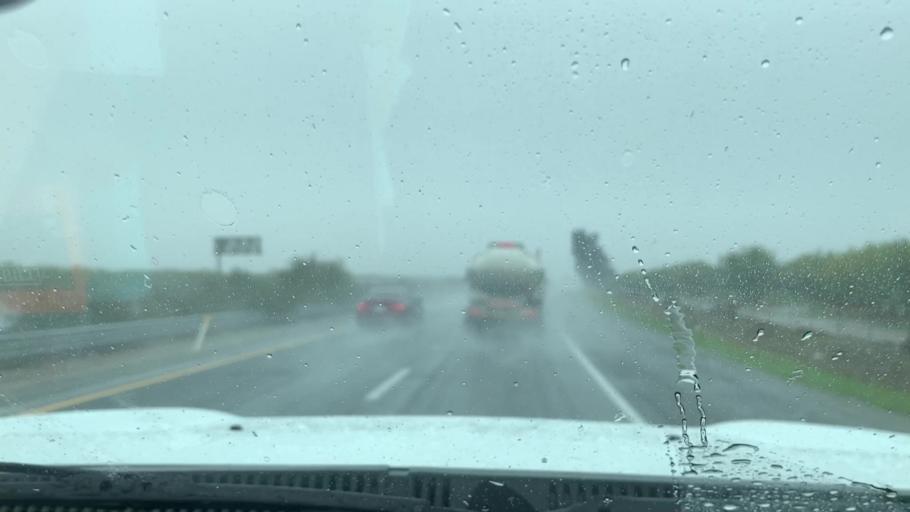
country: US
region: California
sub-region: Tulare County
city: Earlimart
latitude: 35.8432
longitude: -119.2645
